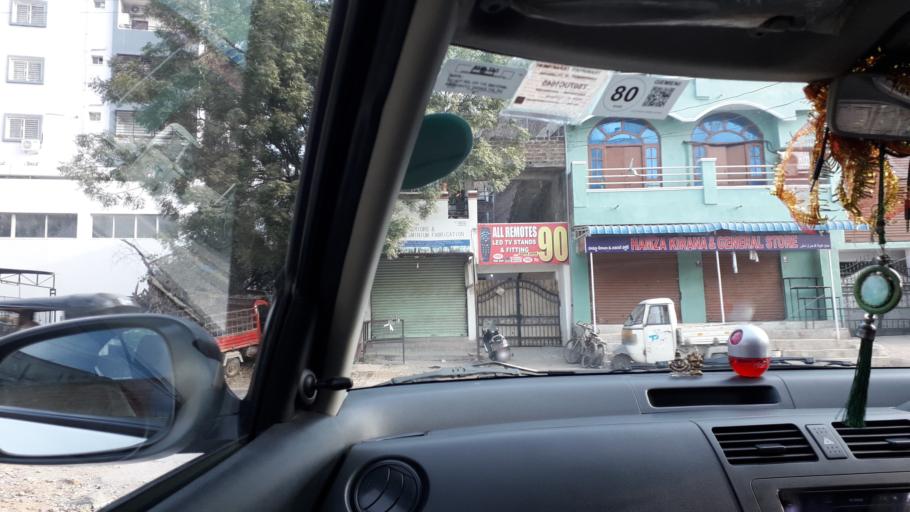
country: IN
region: Telangana
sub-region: Hyderabad
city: Hyderabad
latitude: 17.3938
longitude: 78.3863
